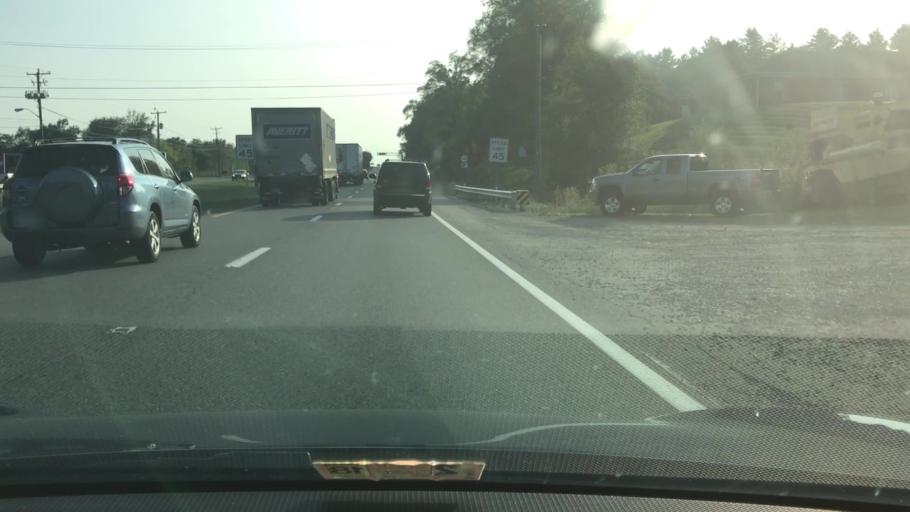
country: US
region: Virginia
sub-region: Botetourt County
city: Laymantown
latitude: 37.3308
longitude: -79.8639
